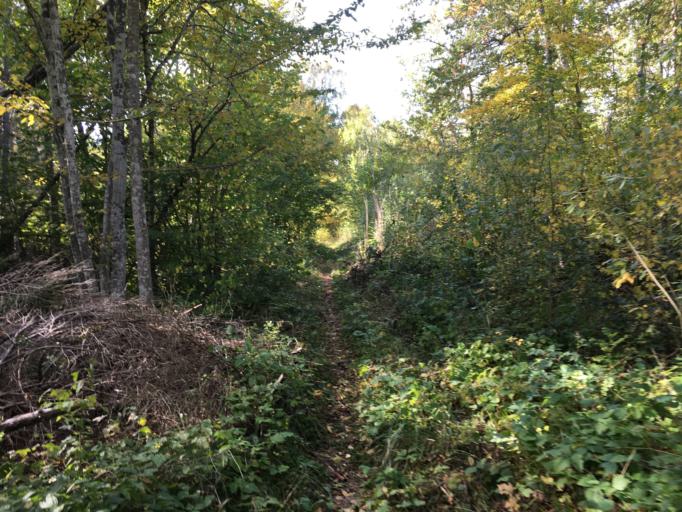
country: SE
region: Kalmar
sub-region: Borgholms Kommun
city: Borgholm
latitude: 56.7477
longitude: 16.6165
